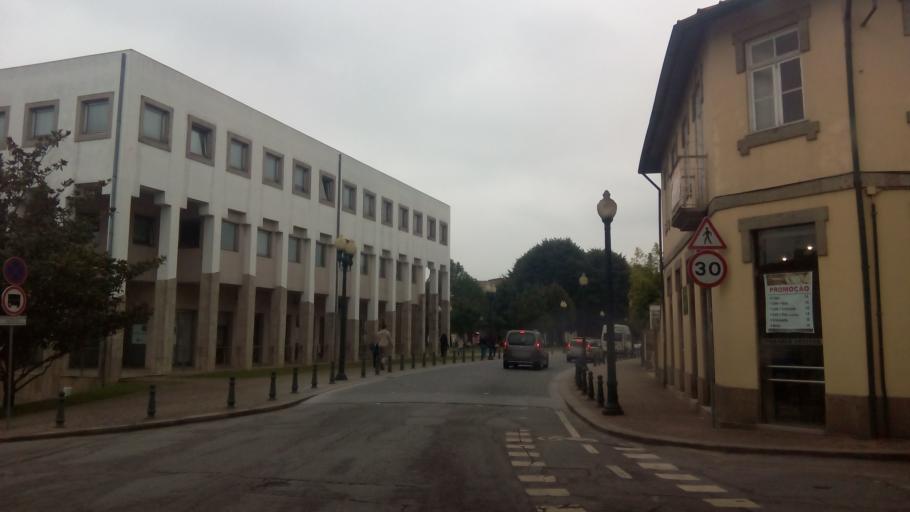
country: PT
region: Porto
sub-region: Paredes
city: Paredes
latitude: 41.2087
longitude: -8.3348
